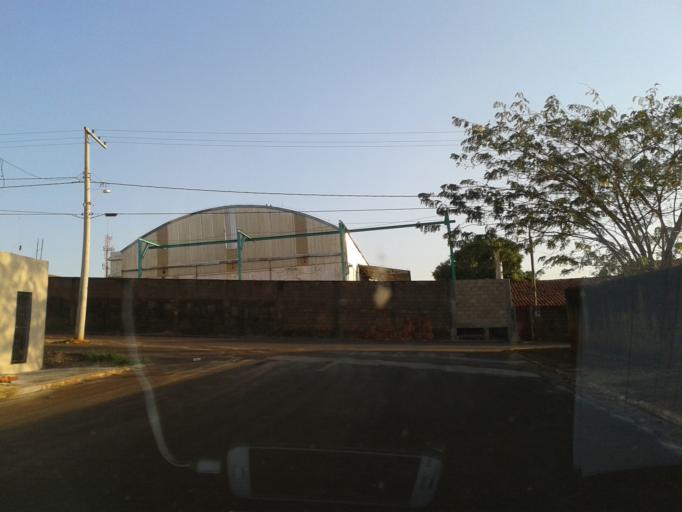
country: BR
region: Minas Gerais
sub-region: Capinopolis
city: Capinopolis
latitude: -18.6839
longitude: -49.5659
